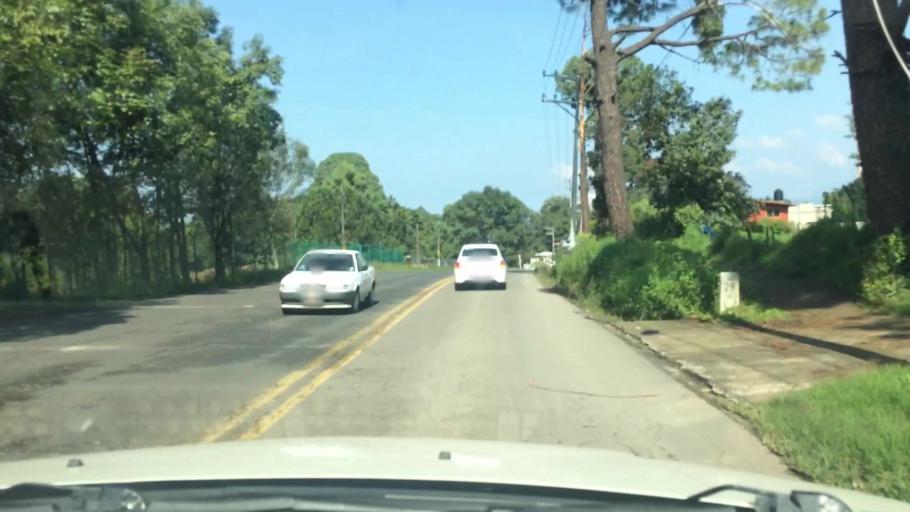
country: MX
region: Mexico
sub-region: Valle de Bravo
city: Casas Viejas
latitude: 19.1600
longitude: -100.1017
